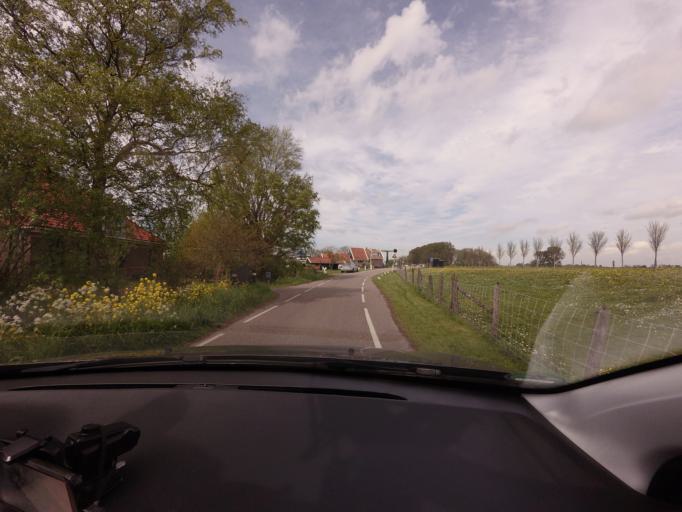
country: NL
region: North Holland
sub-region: Gemeente Beemster
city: Halfweg
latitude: 52.5207
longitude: 4.8705
